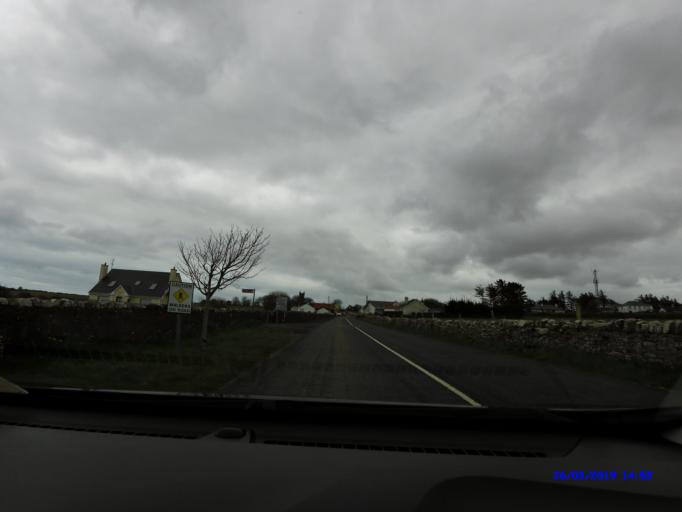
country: IE
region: Connaught
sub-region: Maigh Eo
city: Crossmolina
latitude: 54.2804
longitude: -9.3763
